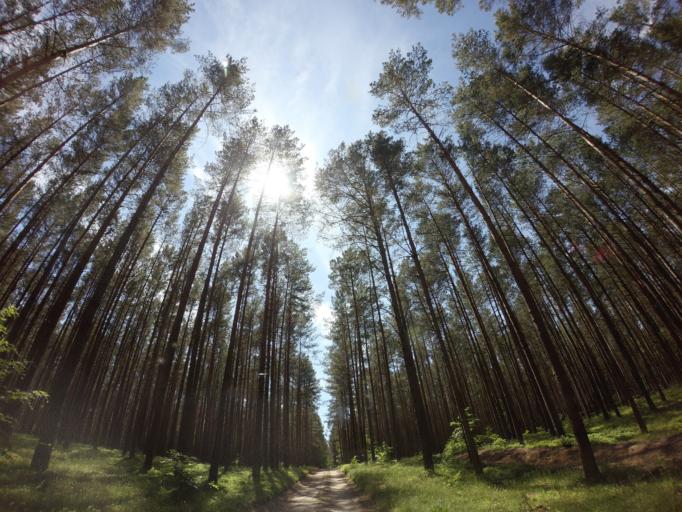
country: PL
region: West Pomeranian Voivodeship
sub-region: Powiat choszczenski
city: Drawno
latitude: 53.1215
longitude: 15.8112
